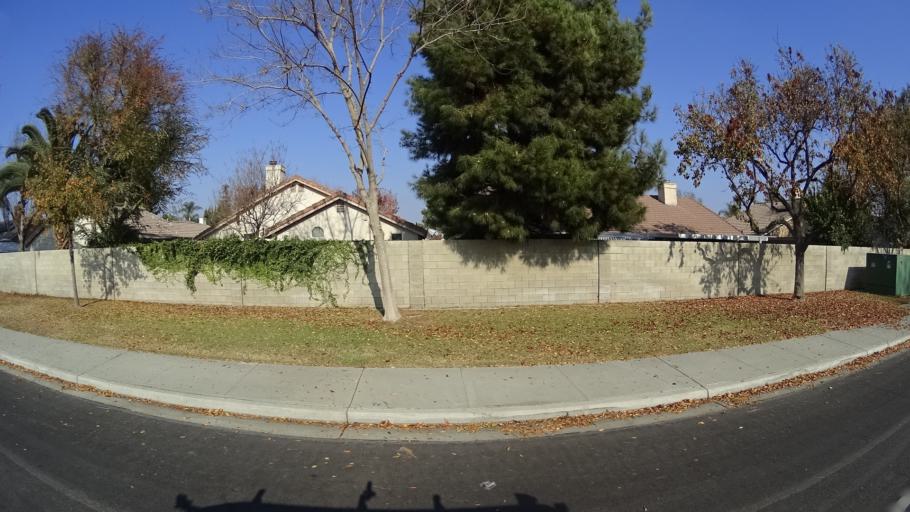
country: US
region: California
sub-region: Kern County
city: Greenacres
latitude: 35.3050
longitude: -119.0820
